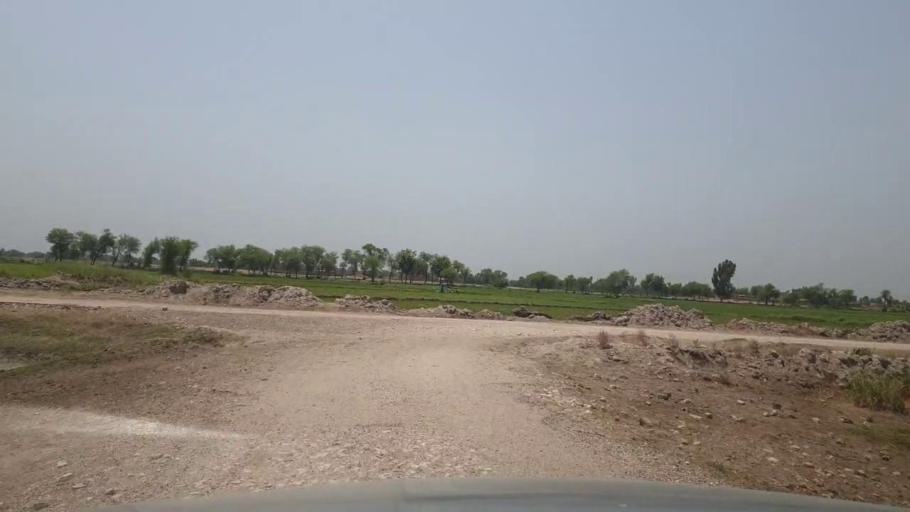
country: PK
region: Sindh
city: Ratodero
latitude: 27.9194
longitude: 68.3623
